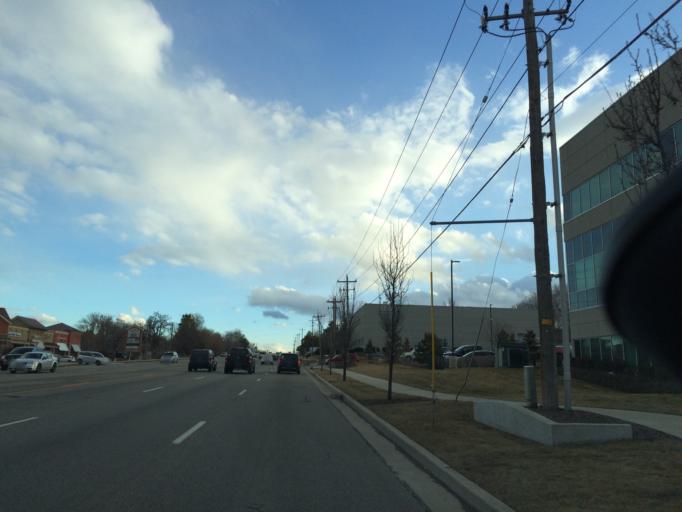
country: US
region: Utah
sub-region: Salt Lake County
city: West Jordan
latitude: 40.6369
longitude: -111.9389
